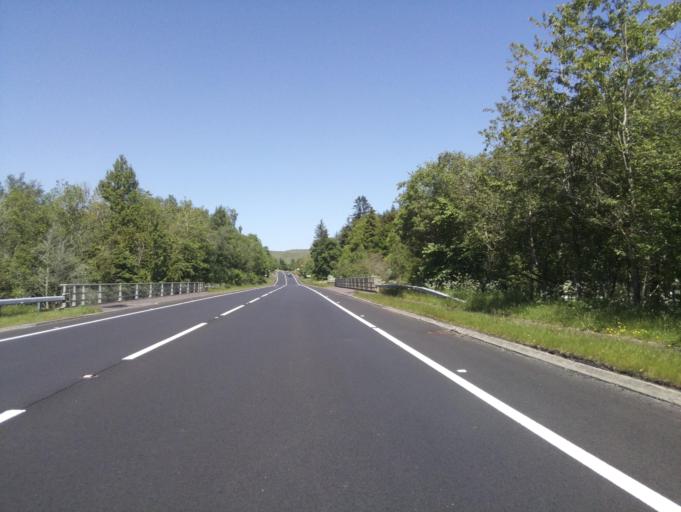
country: GB
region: Scotland
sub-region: The Scottish Borders
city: Hawick
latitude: 55.3345
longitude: -2.9402
